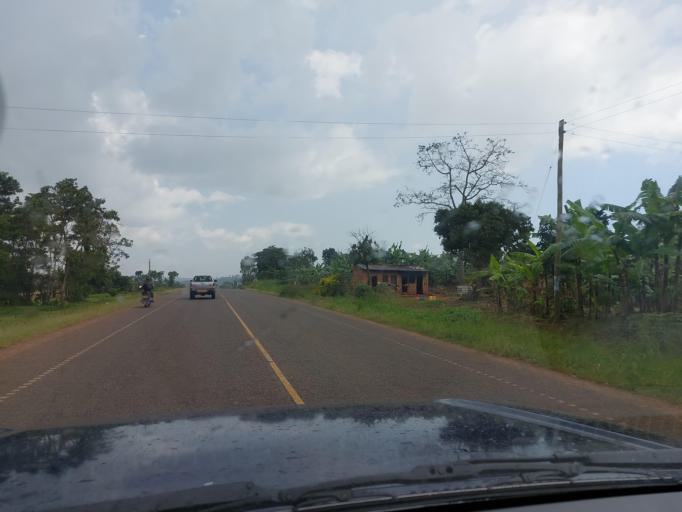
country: UG
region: Central Region
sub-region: Buikwe District
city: Buikwe
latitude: 0.2406
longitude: 32.9380
